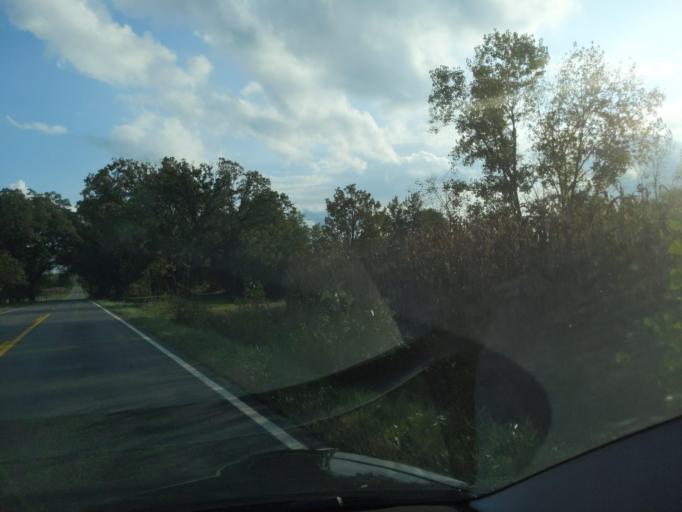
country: US
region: Michigan
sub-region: Jackson County
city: Jackson
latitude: 42.3415
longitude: -84.4629
